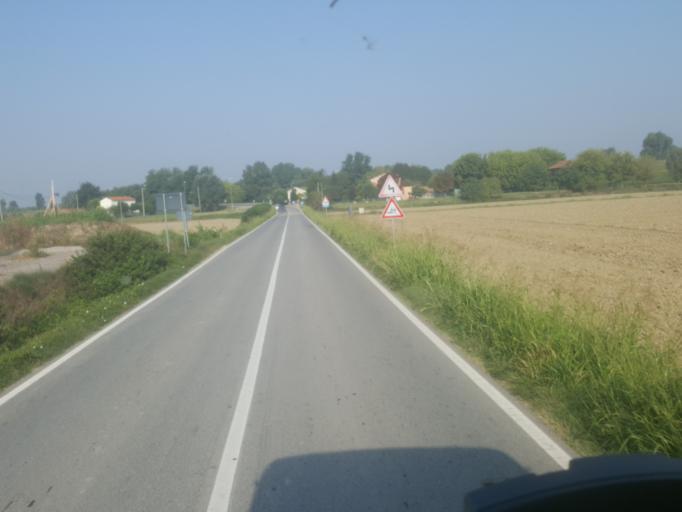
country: IT
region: Emilia-Romagna
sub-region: Provincia di Ravenna
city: Voltana
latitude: 44.5535
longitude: 11.9410
